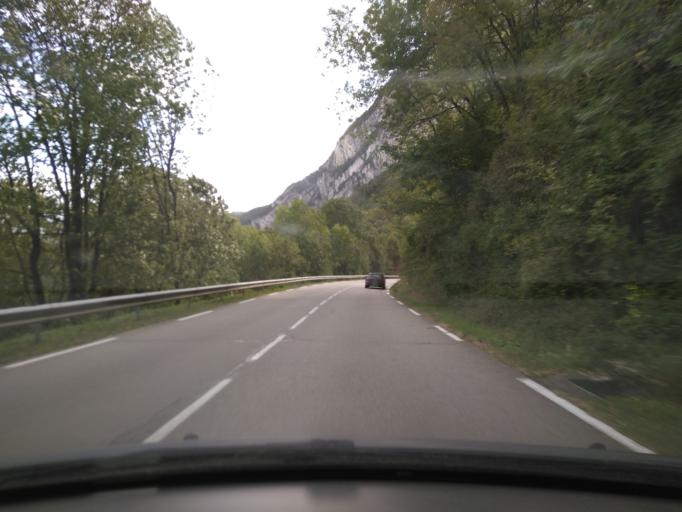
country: FR
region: Rhone-Alpes
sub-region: Departement de l'Isere
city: Sassenage
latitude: 45.2149
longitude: 5.6552
